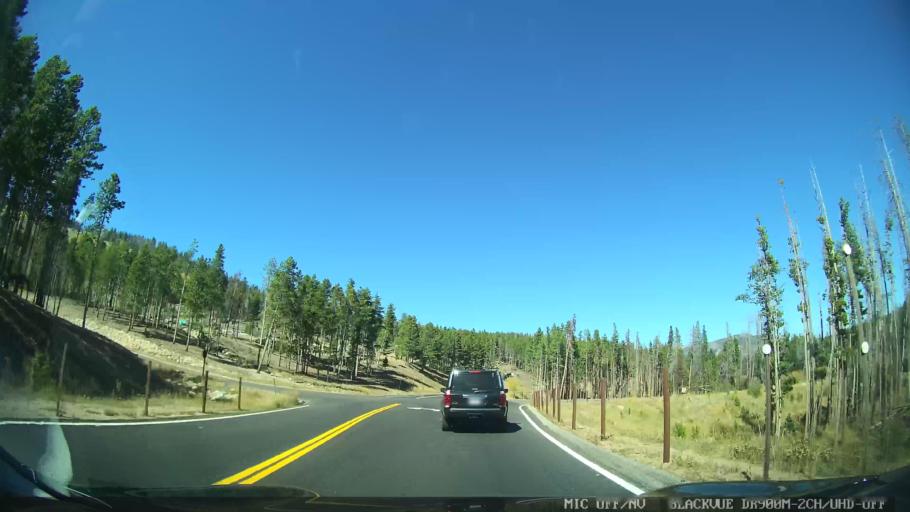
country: US
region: Colorado
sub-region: Larimer County
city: Estes Park
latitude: 40.3291
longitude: -105.5996
